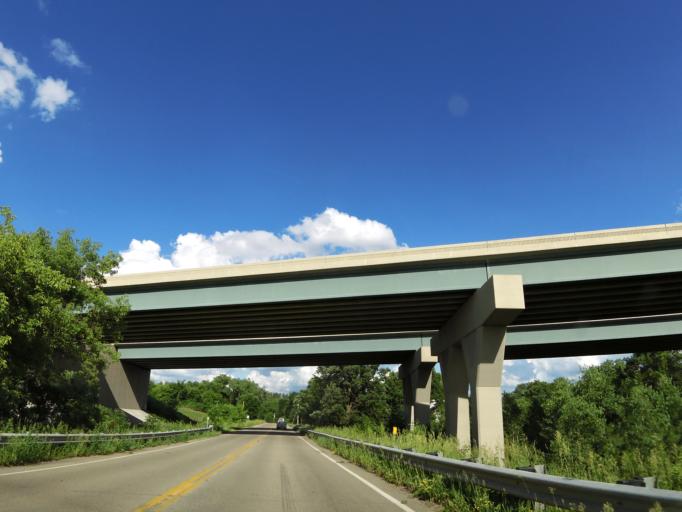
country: US
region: Minnesota
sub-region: Carver County
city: Chaska
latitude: 44.8006
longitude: -93.6304
